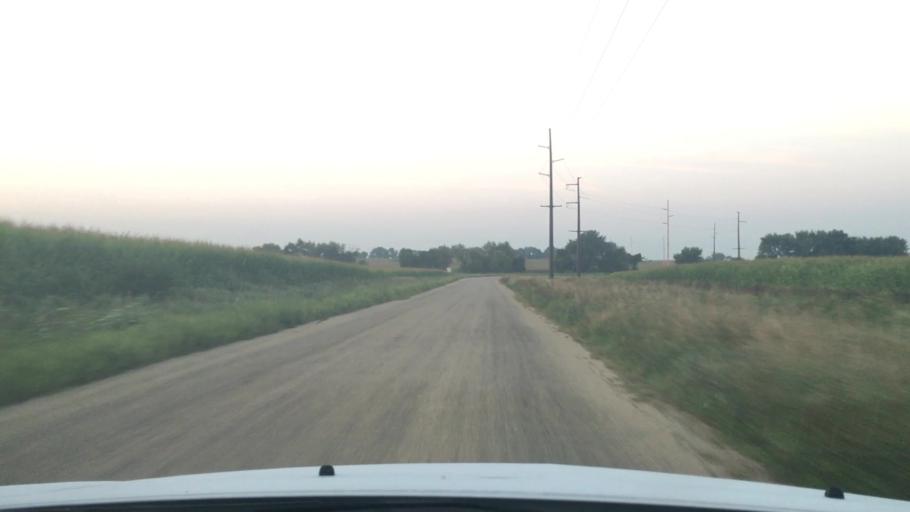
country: US
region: Illinois
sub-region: Ogle County
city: Rochelle
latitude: 41.8938
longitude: -88.9997
